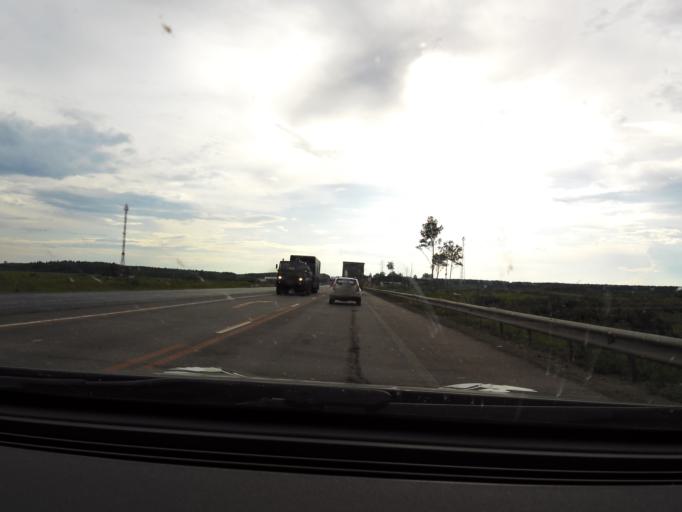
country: RU
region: Vladimir
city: Stepantsevo
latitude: 56.2337
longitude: 41.8135
